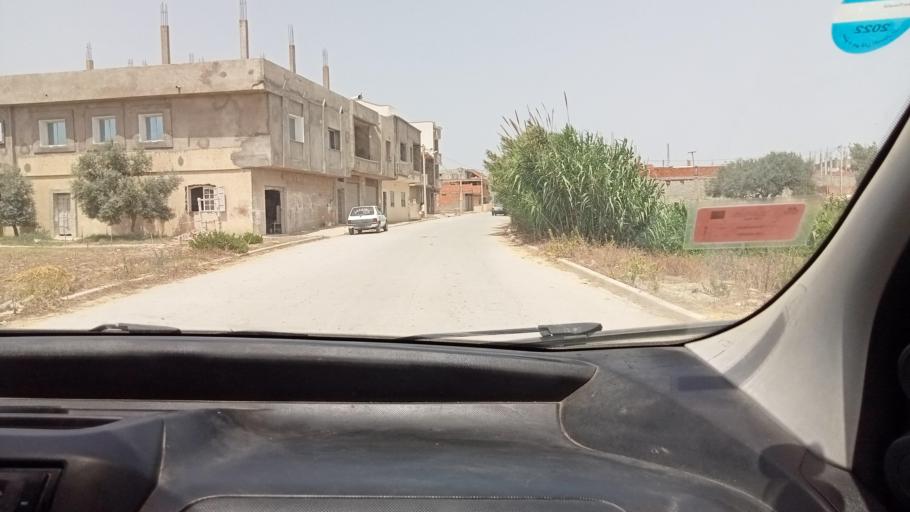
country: TN
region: Nabul
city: Qulaybiyah
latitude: 36.8623
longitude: 11.0858
